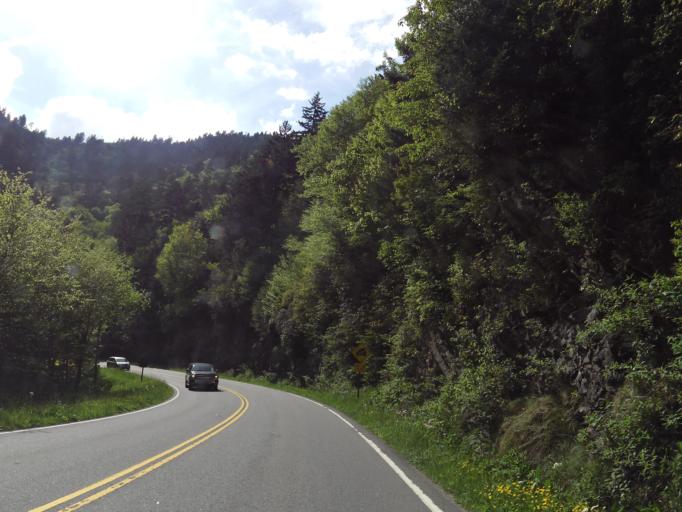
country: US
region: Tennessee
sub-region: Sevier County
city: Gatlinburg
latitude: 35.6249
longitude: -83.4181
